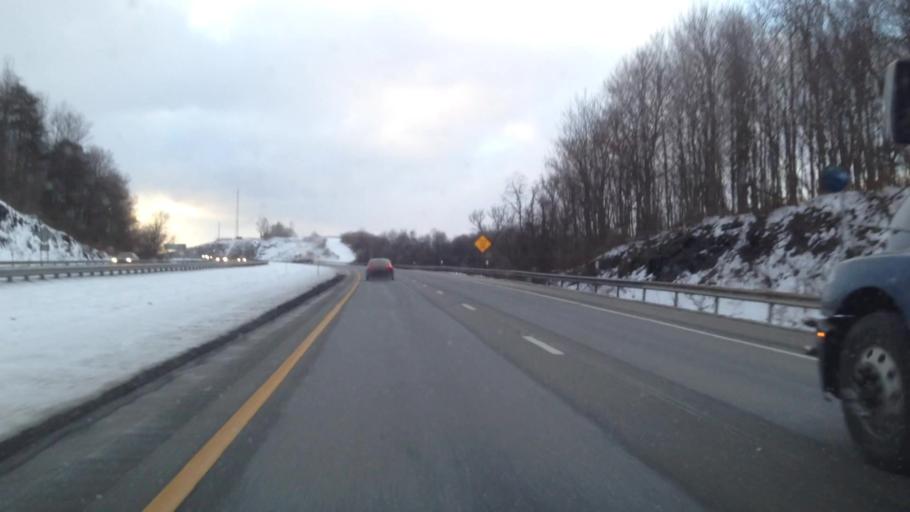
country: US
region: New York
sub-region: Herkimer County
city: Little Falls
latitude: 43.0113
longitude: -74.8488
